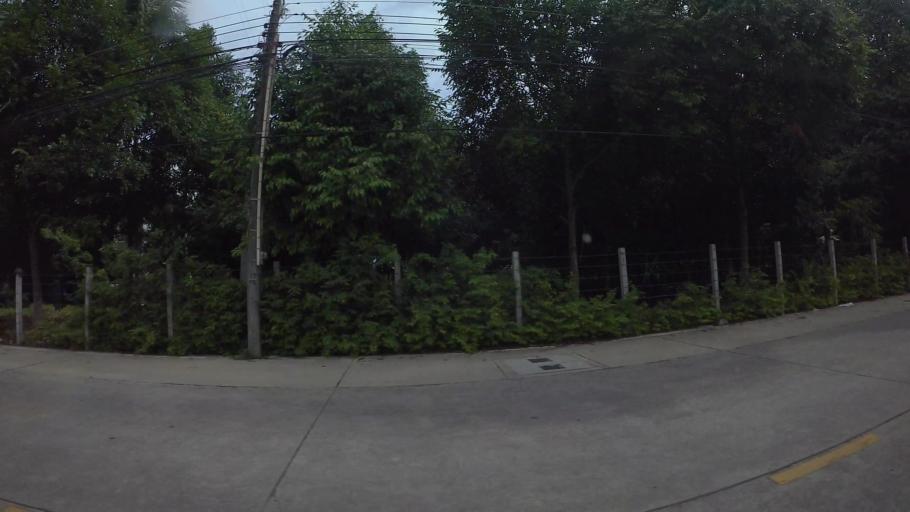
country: TH
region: Chon Buri
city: Si Racha
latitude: 13.1507
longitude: 100.9755
